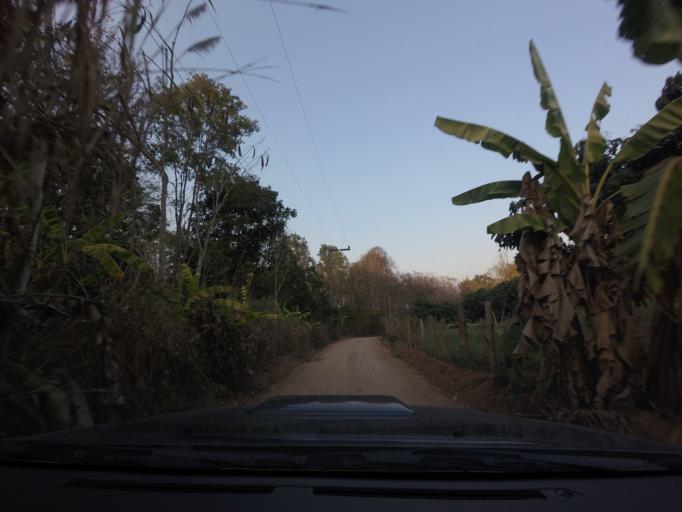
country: TH
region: Chiang Mai
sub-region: Amphoe Chiang Dao
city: Chiang Dao
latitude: 19.3667
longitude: 98.9434
